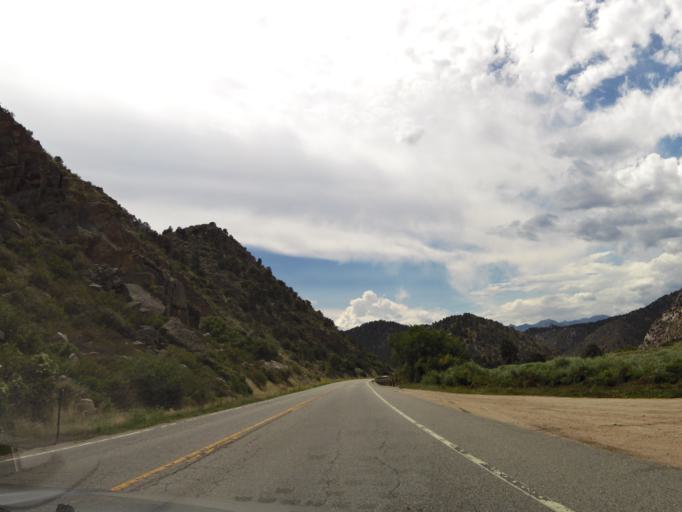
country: US
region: Colorado
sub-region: Custer County
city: Westcliffe
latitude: 38.3928
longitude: -105.6384
